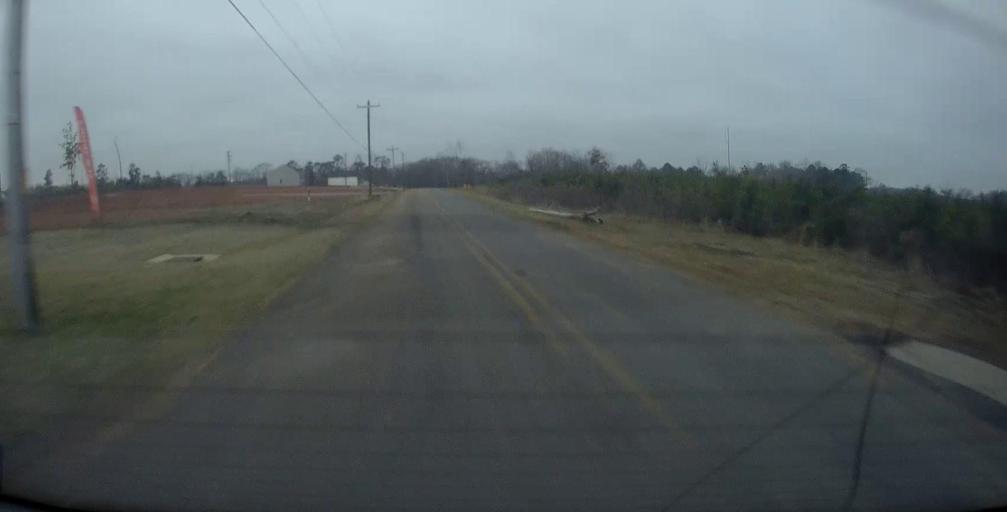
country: US
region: Georgia
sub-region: Bibb County
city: West Point
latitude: 32.9255
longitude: -83.7883
